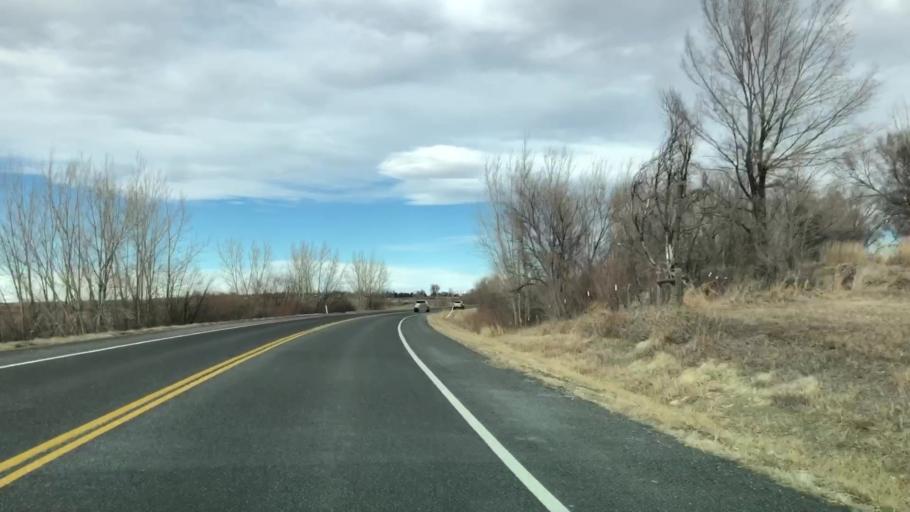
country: US
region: Colorado
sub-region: Weld County
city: Windsor
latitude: 40.5117
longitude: -104.9273
